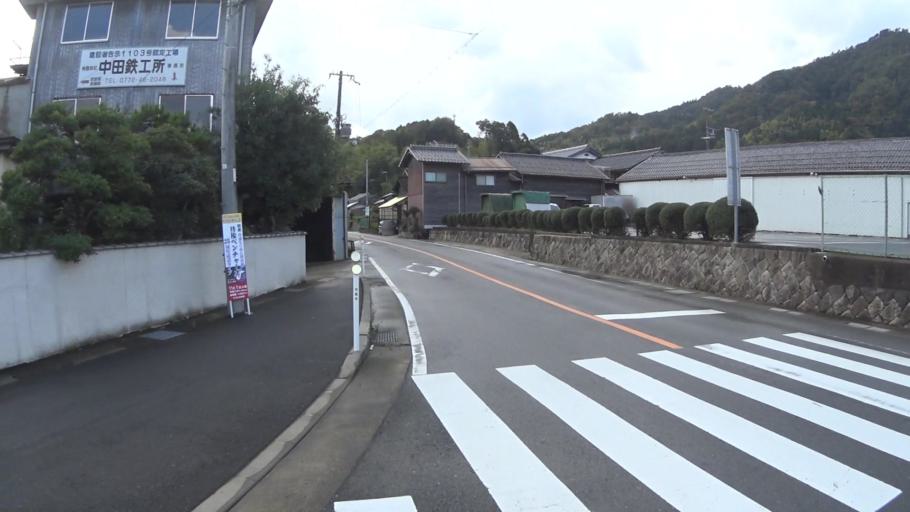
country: JP
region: Kyoto
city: Miyazu
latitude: 35.5537
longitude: 135.1383
